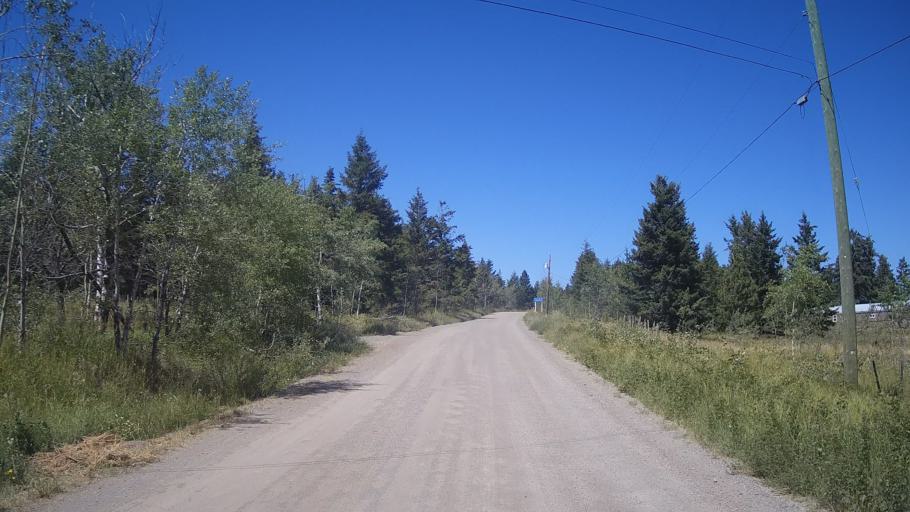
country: CA
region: British Columbia
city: Cache Creek
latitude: 51.1469
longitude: -121.5040
